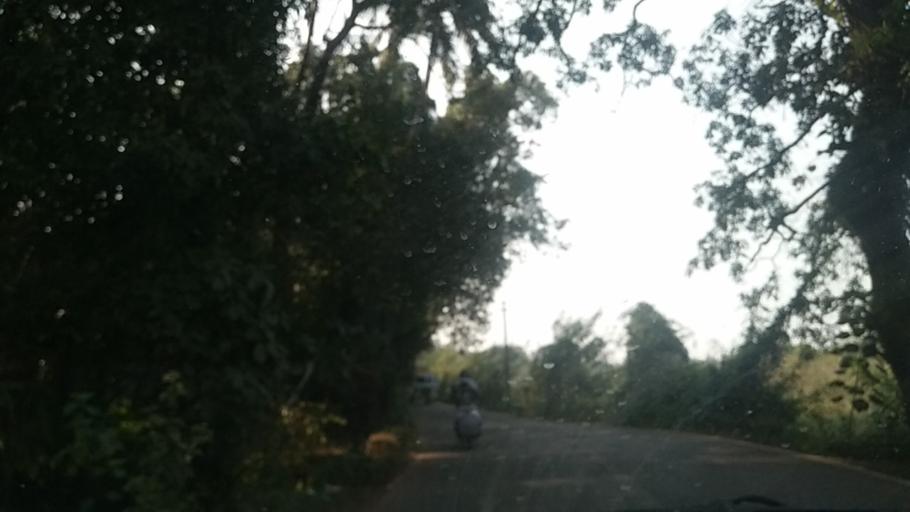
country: IN
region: Goa
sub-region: North Goa
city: Pernem
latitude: 15.7128
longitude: 73.8101
